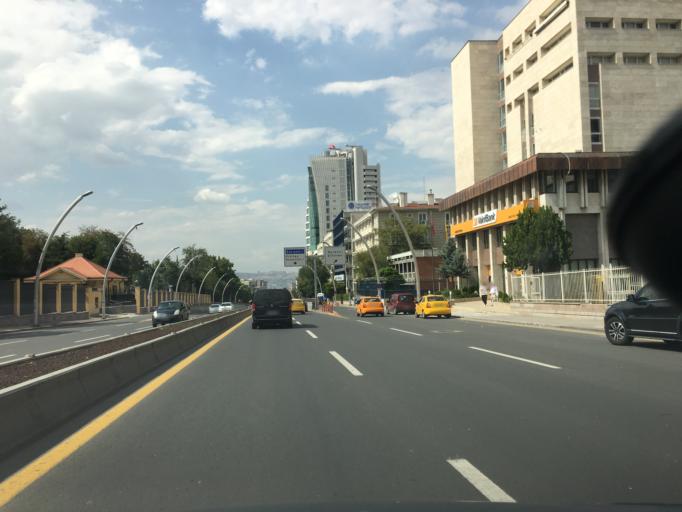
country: TR
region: Ankara
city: Cankaya
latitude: 39.9060
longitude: 32.8578
